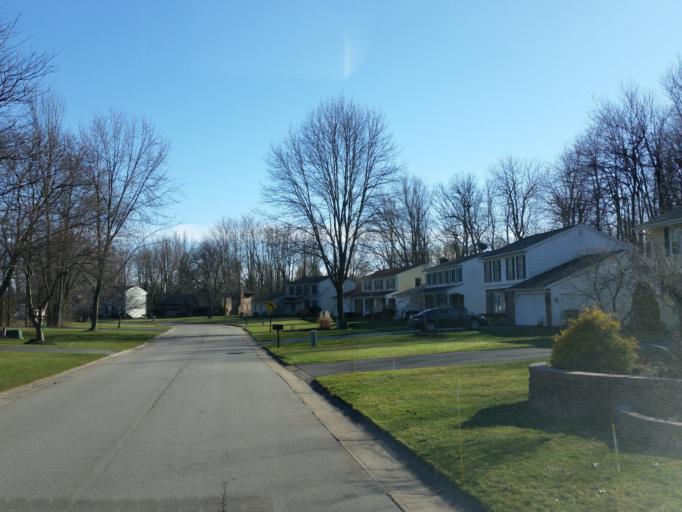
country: US
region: New York
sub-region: Monroe County
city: North Gates
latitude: 43.1124
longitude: -77.7490
